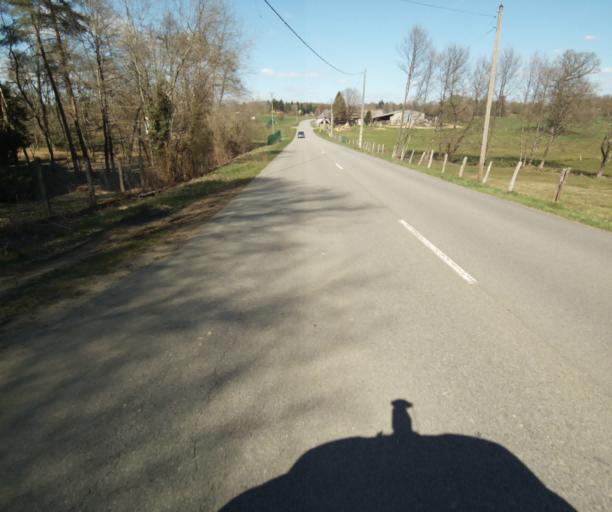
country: FR
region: Limousin
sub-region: Departement de la Correze
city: Saint-Mexant
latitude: 45.2916
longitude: 1.6687
